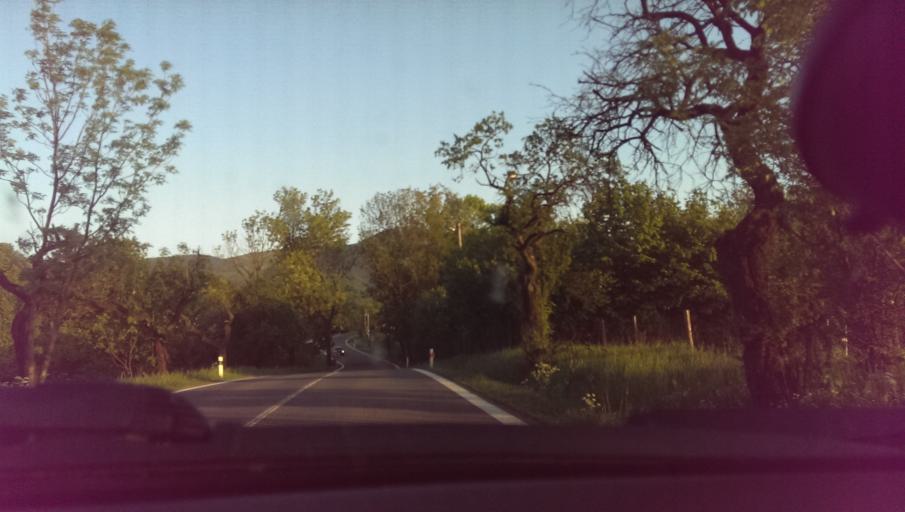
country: CZ
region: Moravskoslezsky
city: Frenstat pod Radhostem
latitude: 49.5313
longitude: 18.2035
